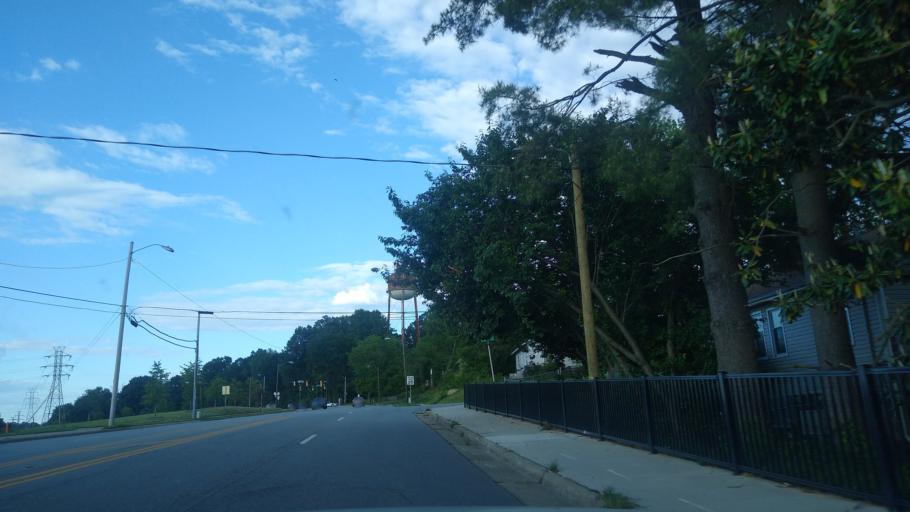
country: US
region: North Carolina
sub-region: Guilford County
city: Greensboro
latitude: 36.0967
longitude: -79.7777
